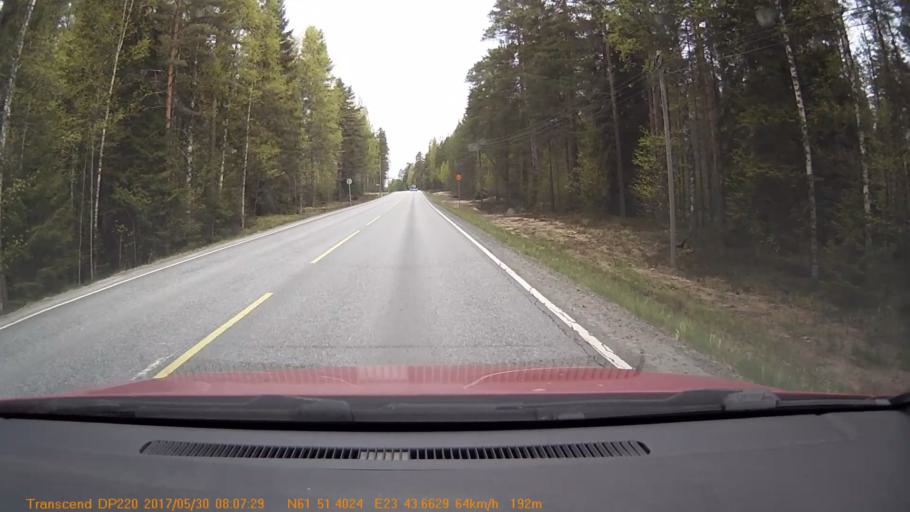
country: FI
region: Pirkanmaa
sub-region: Tampere
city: Kuru
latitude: 61.8564
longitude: 23.7277
